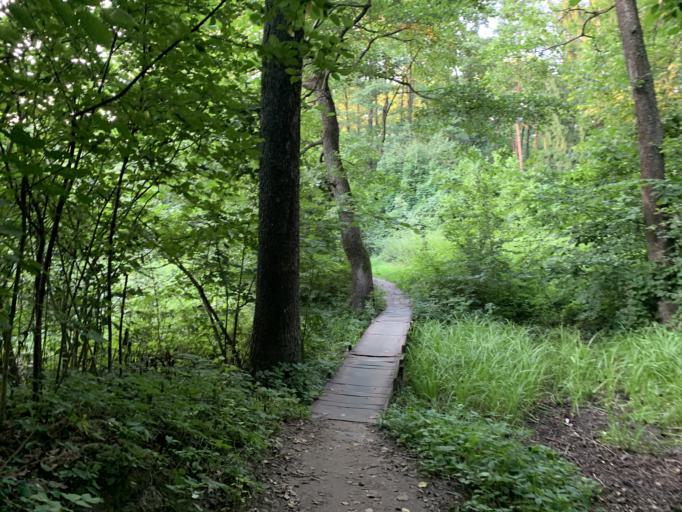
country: BY
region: Minsk
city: Nyasvizh
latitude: 53.2057
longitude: 26.6512
